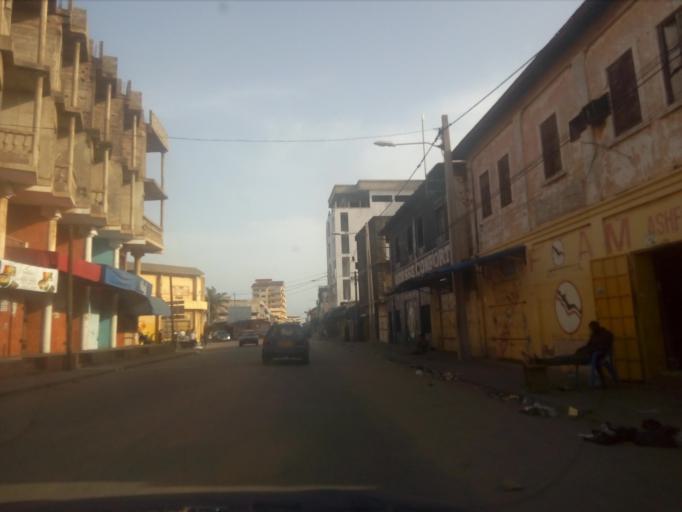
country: TG
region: Maritime
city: Lome
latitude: 6.1311
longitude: 1.2279
